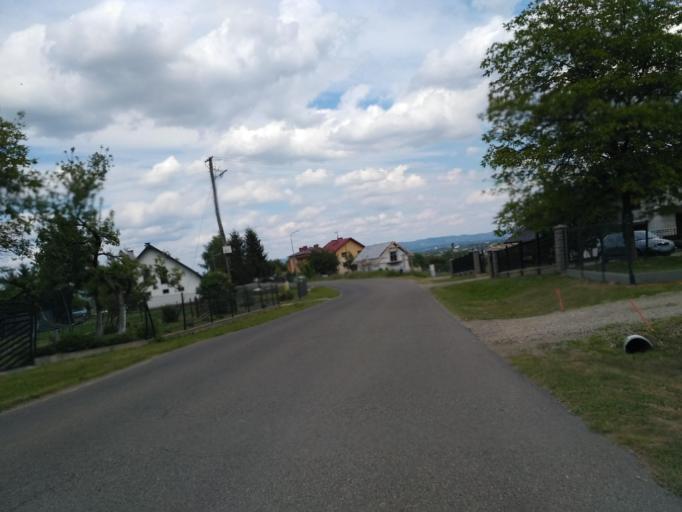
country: PL
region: Subcarpathian Voivodeship
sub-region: Powiat krosnienski
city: Chorkowka
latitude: 49.6417
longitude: 21.6662
